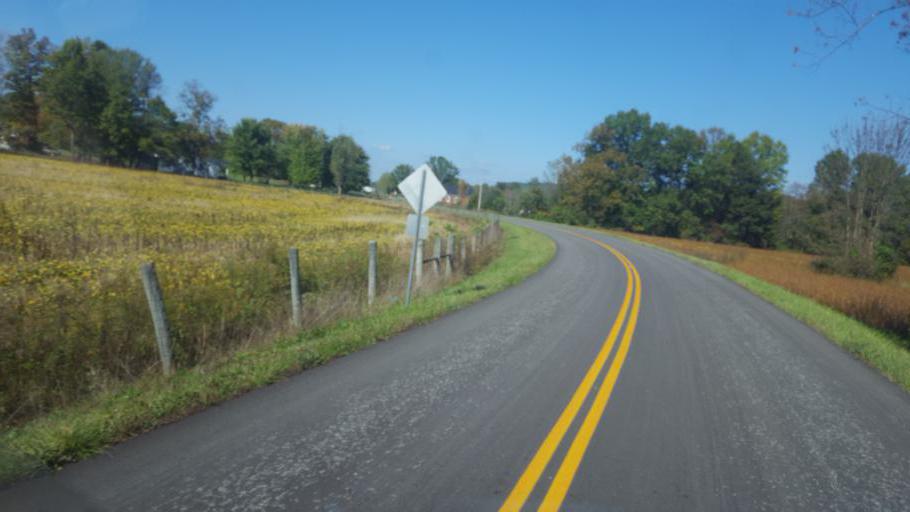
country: US
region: Kentucky
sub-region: Fleming County
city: Flemingsburg
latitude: 38.4503
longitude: -83.5826
